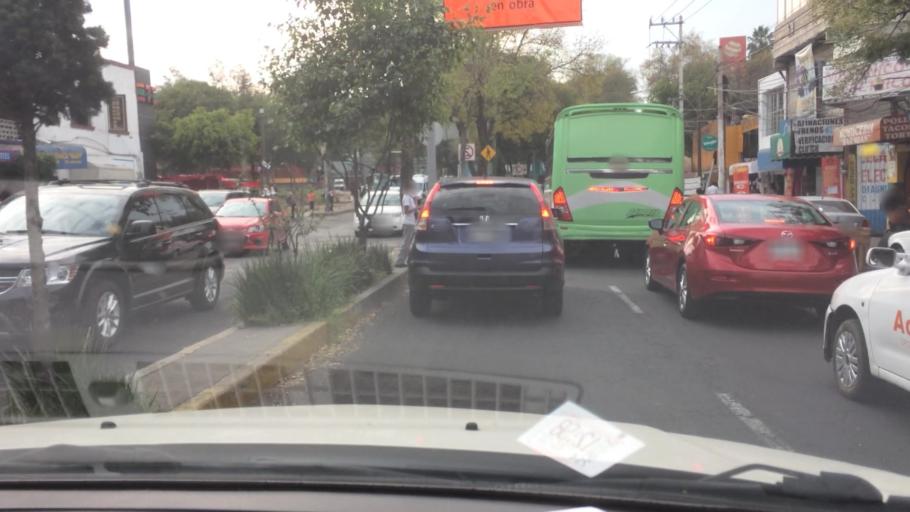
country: MX
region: Mexico City
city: Tlalpan
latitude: 19.2953
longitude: -99.1816
